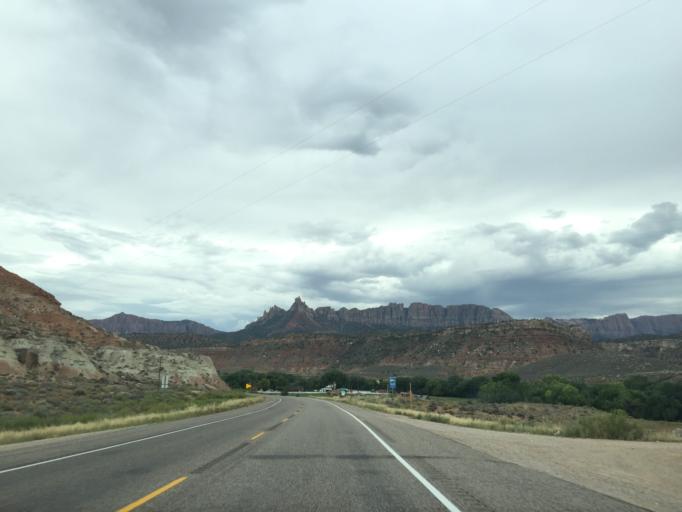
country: US
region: Utah
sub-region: Washington County
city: Hildale
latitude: 37.1647
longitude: -113.0611
